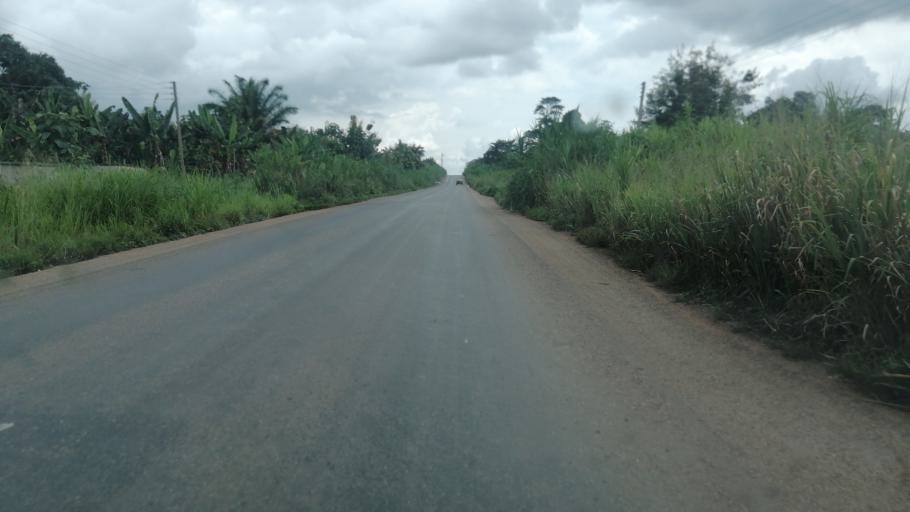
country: GH
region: Western
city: Bibiani
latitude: 6.8700
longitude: -2.4380
